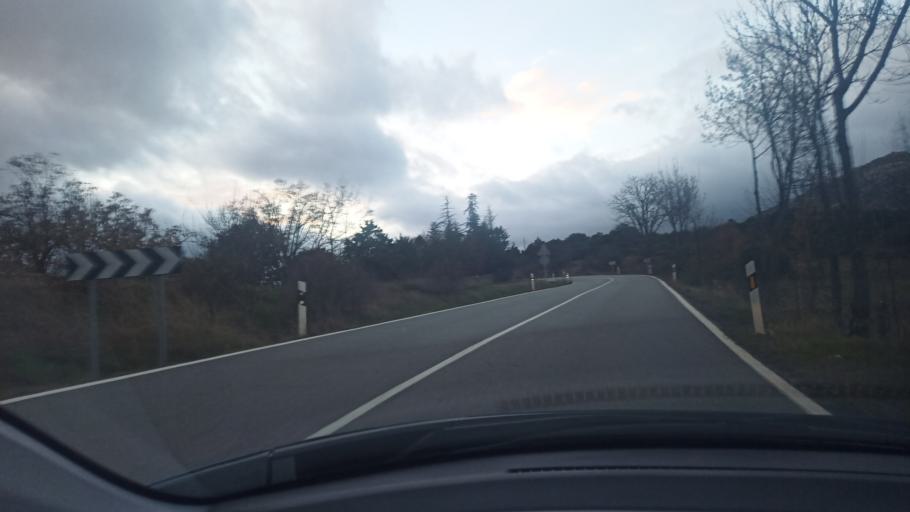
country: ES
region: Madrid
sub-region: Provincia de Madrid
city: El Escorial
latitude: 40.5374
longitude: -4.1322
